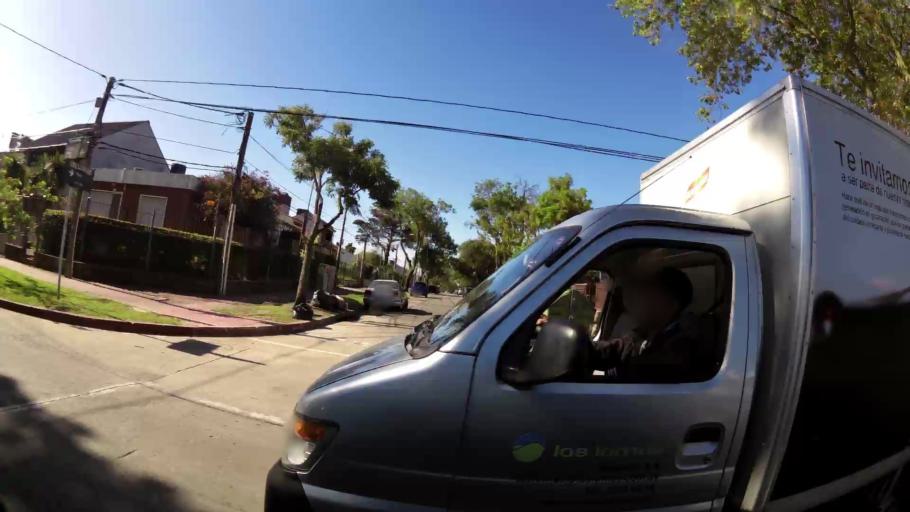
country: UY
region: Canelones
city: Paso de Carrasco
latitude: -34.8907
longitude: -56.0884
